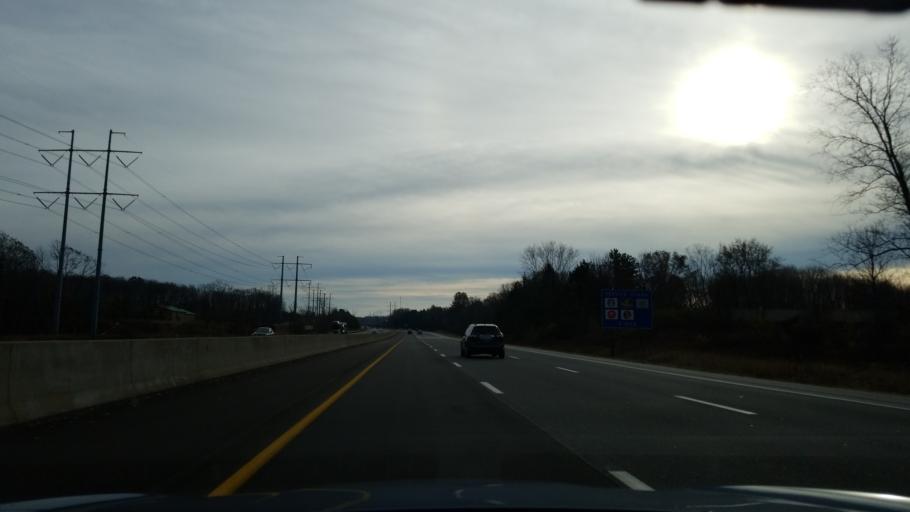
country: US
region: Ohio
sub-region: Cuyahoga County
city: Broadview Heights
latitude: 41.2995
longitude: -81.6973
